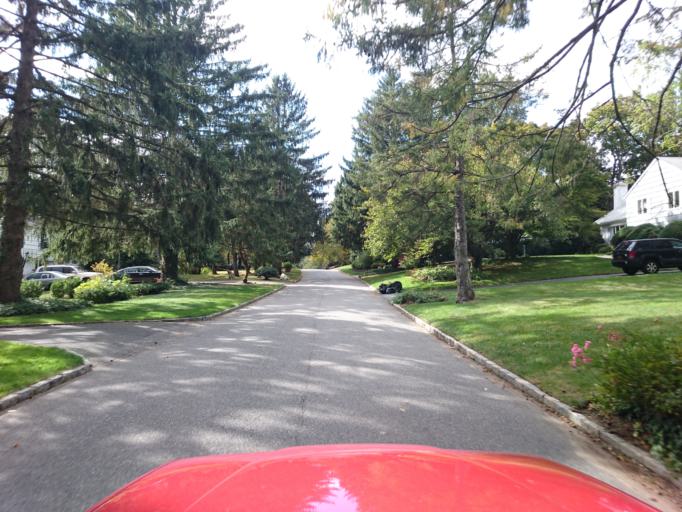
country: US
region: New York
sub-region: Nassau County
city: Locust Valley
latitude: 40.8775
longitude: -73.6047
